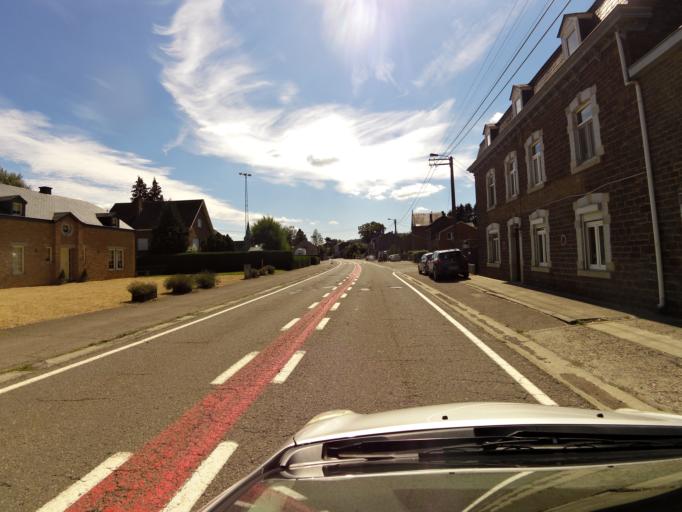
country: BE
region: Wallonia
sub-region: Province du Luxembourg
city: Rendeux
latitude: 50.2445
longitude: 5.4968
